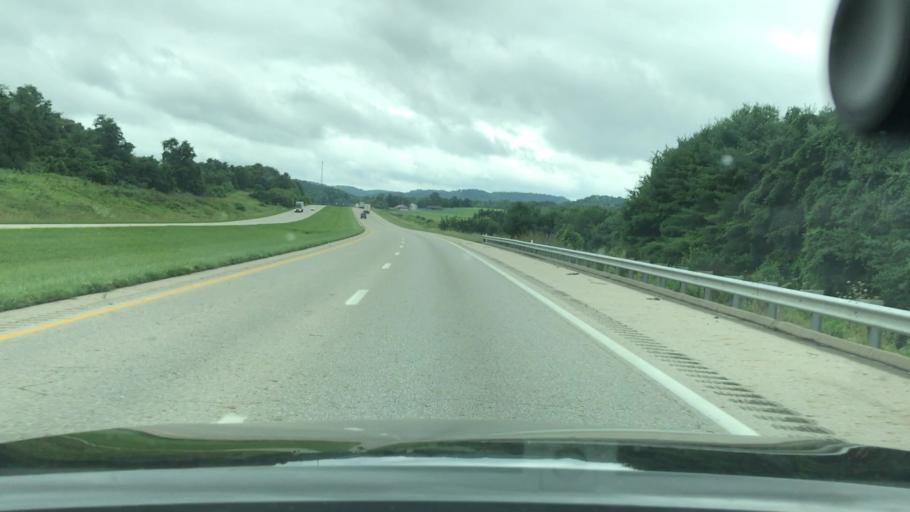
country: US
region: Ohio
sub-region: Ross County
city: Chillicothe
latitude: 39.2635
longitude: -82.8686
